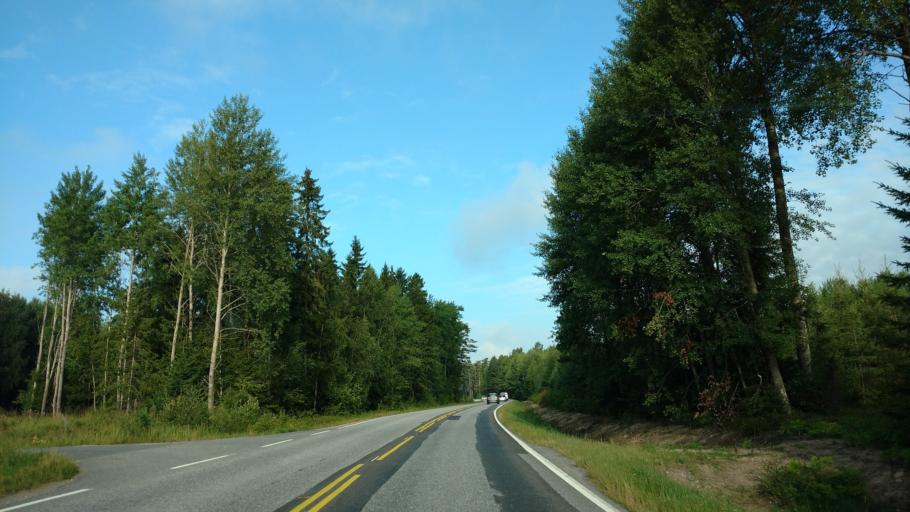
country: FI
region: Varsinais-Suomi
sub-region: Aboland-Turunmaa
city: Dragsfjaerd
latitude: 60.1029
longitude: 22.5825
